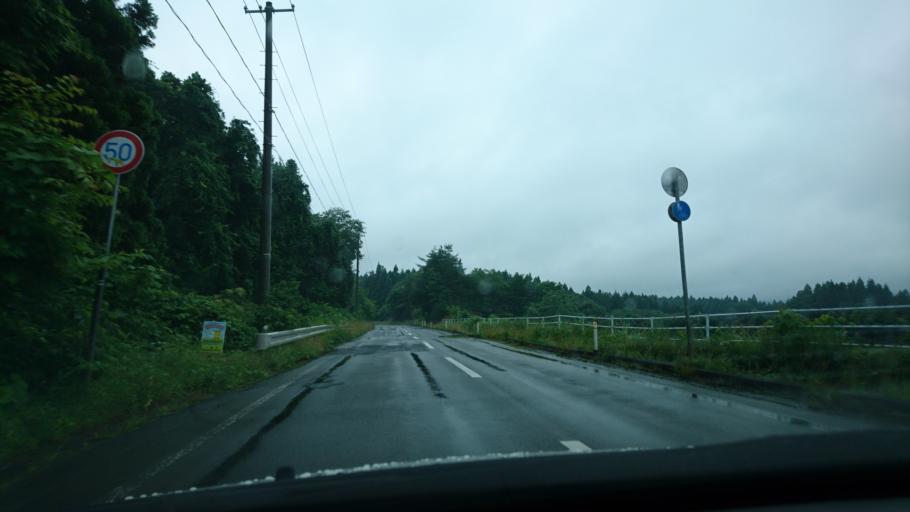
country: JP
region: Iwate
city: Ichinoseki
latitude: 38.9356
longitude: 141.0520
